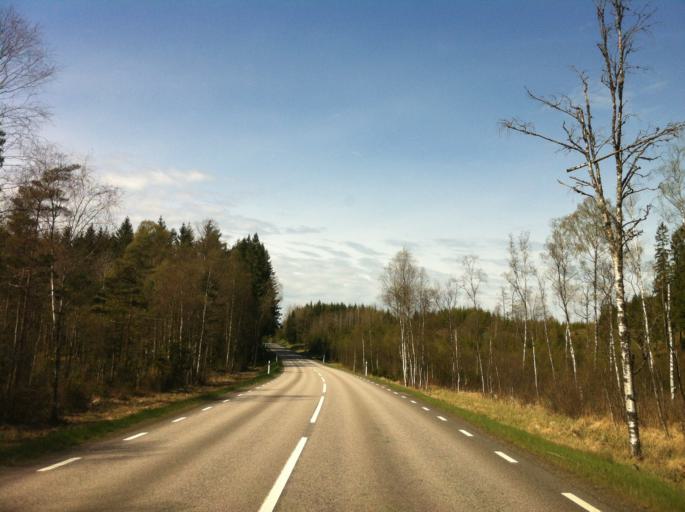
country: SE
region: Vaestra Goetaland
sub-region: Marks Kommun
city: Kinna
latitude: 57.2056
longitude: 12.8238
